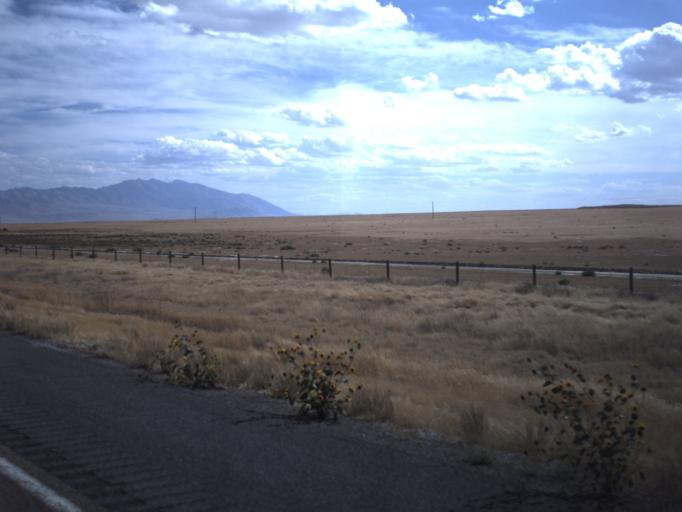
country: US
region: Utah
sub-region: Tooele County
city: Grantsville
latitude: 40.8036
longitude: -112.8563
